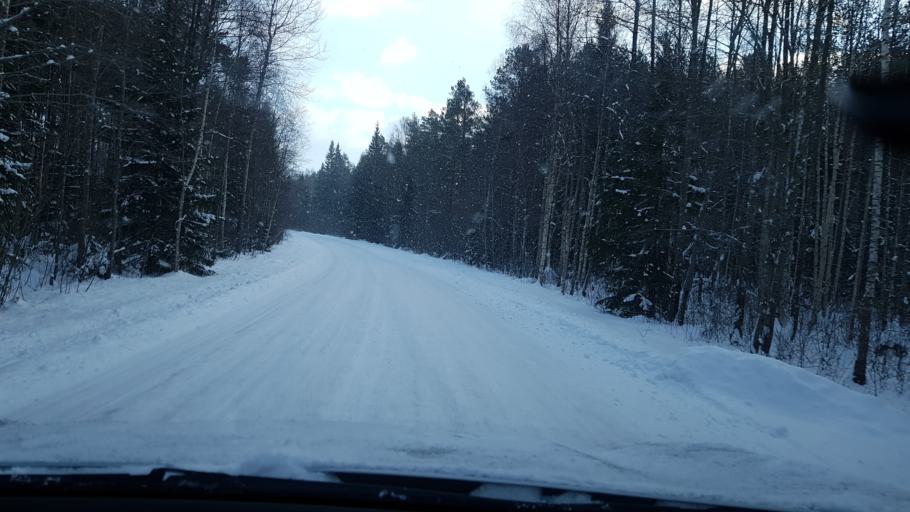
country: EE
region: Harju
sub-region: Nissi vald
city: Turba
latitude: 59.1737
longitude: 24.1337
